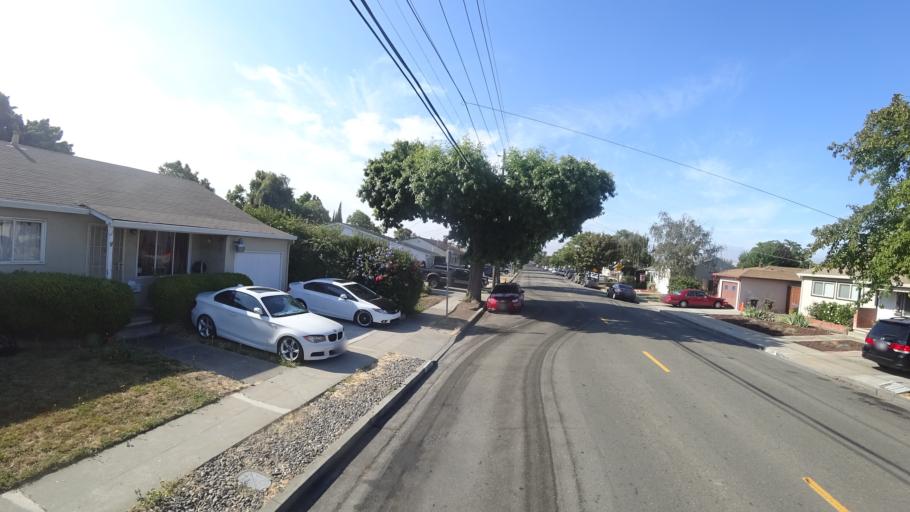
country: US
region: California
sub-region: Alameda County
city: Hayward
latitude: 37.6459
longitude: -122.0835
